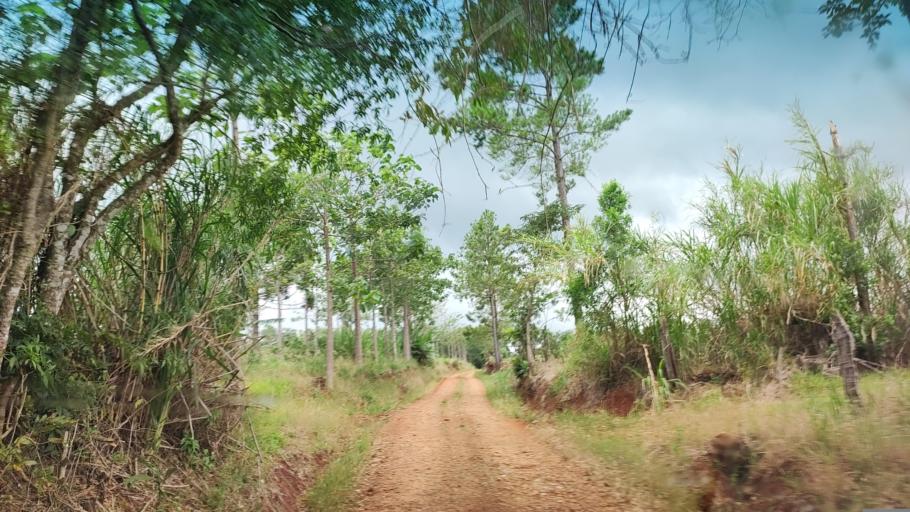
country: AR
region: Misiones
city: Dos de Mayo
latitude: -27.0042
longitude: -54.6245
